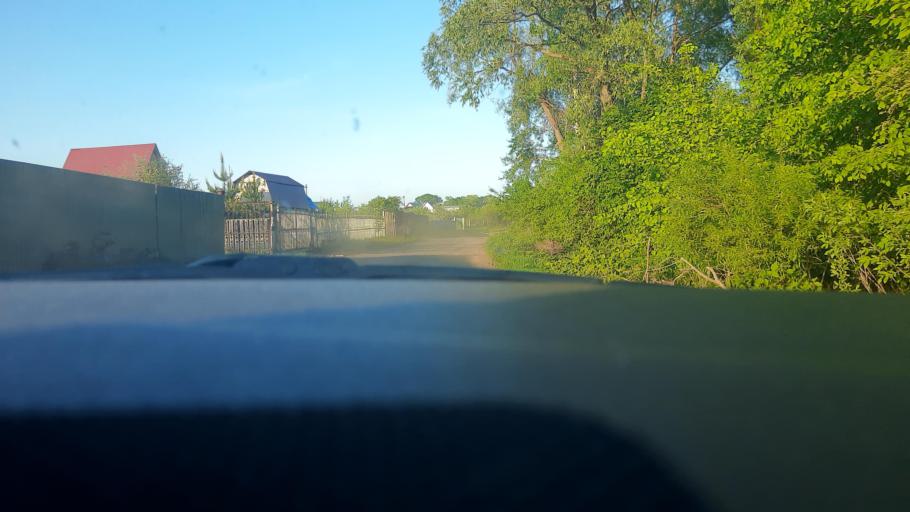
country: RU
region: Bashkortostan
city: Chishmy
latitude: 54.6305
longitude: 55.5254
